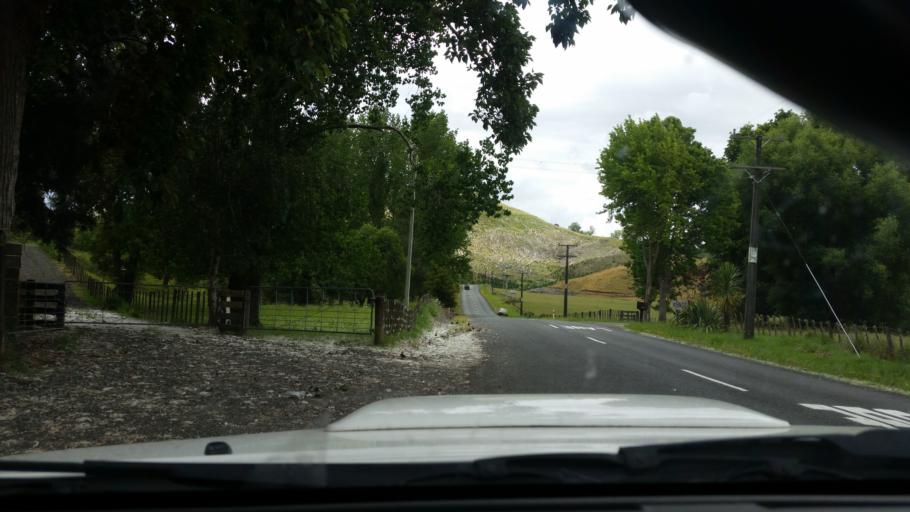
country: NZ
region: Northland
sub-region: Kaipara District
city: Dargaville
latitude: -35.7453
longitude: 173.8773
